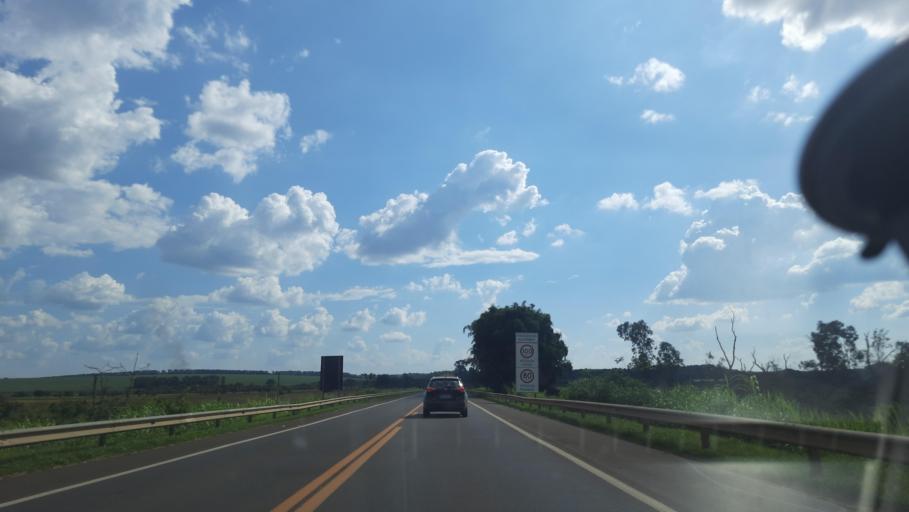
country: BR
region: Sao Paulo
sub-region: Casa Branca
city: Casa Branca
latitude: -21.7446
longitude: -46.9844
